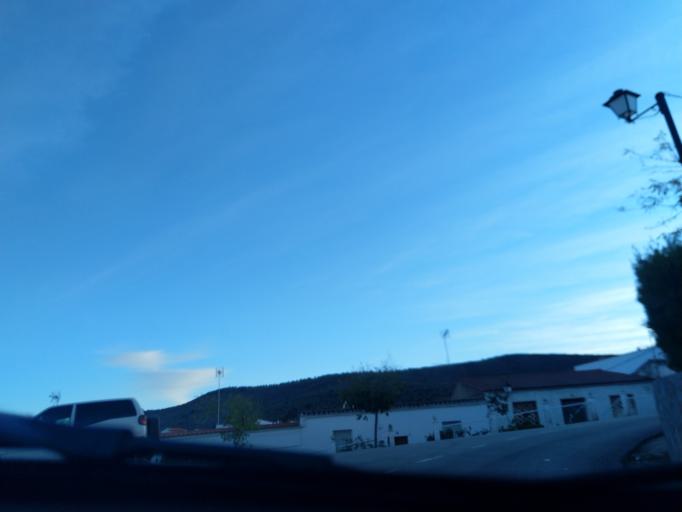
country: ES
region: Extremadura
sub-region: Provincia de Badajoz
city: Reina
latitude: 38.1556
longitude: -5.8969
